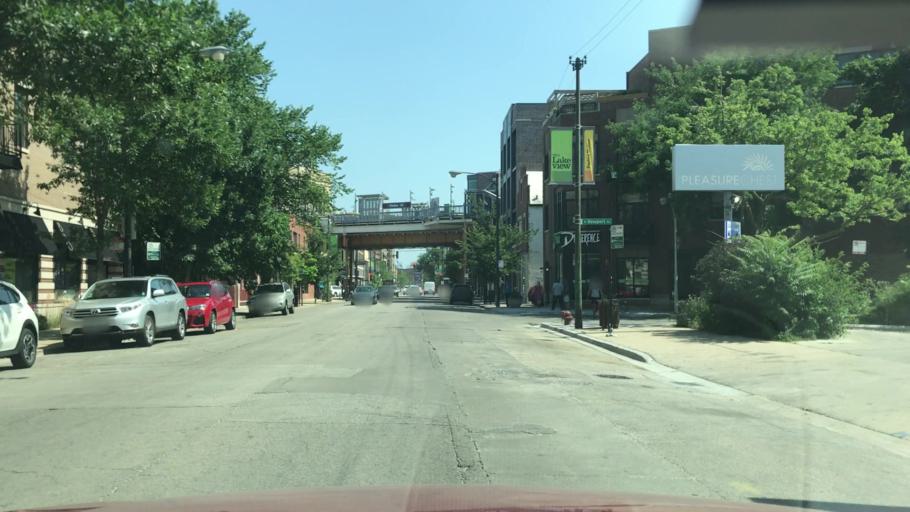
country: US
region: Illinois
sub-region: Cook County
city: Lincolnwood
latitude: 41.9446
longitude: -87.6721
